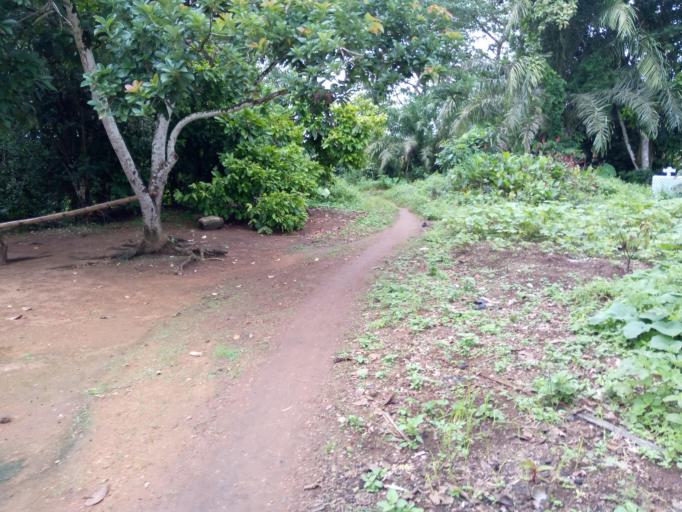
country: SL
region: Eastern Province
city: Buedu
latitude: 8.4531
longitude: -10.3309
